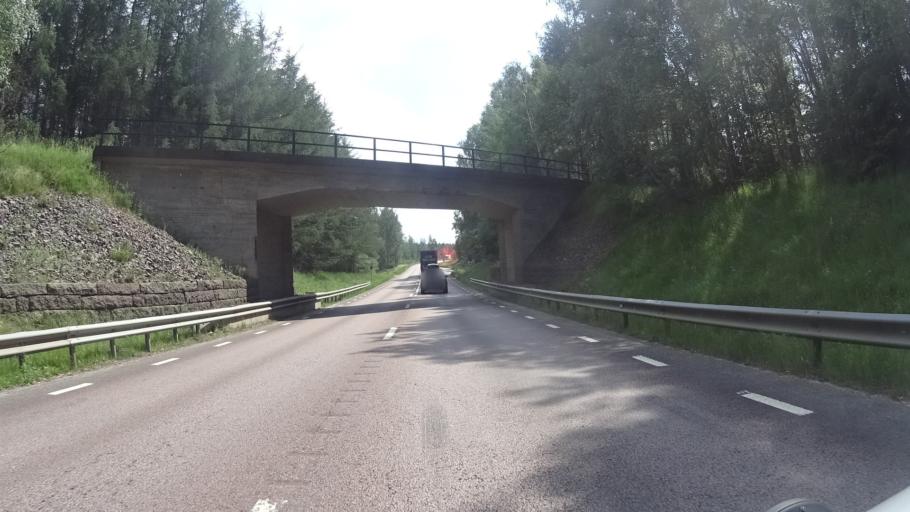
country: SE
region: Kalmar
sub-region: Hultsfreds Kommun
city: Hultsfred
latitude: 57.4415
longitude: 15.8353
